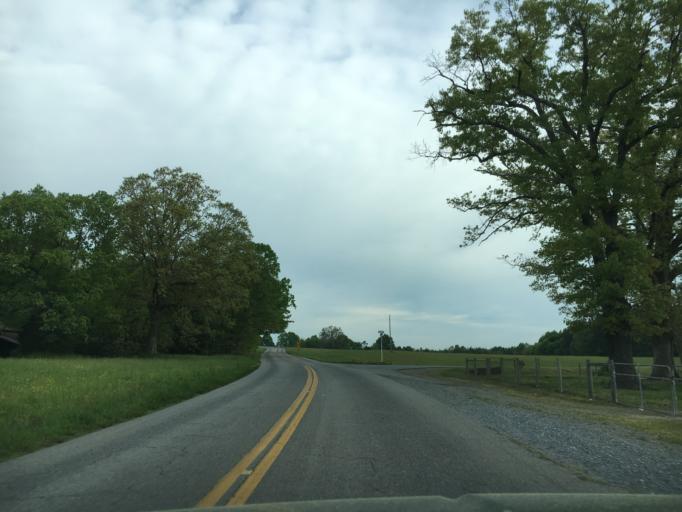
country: US
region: Virginia
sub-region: Halifax County
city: Halifax
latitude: 36.9074
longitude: -78.9145
